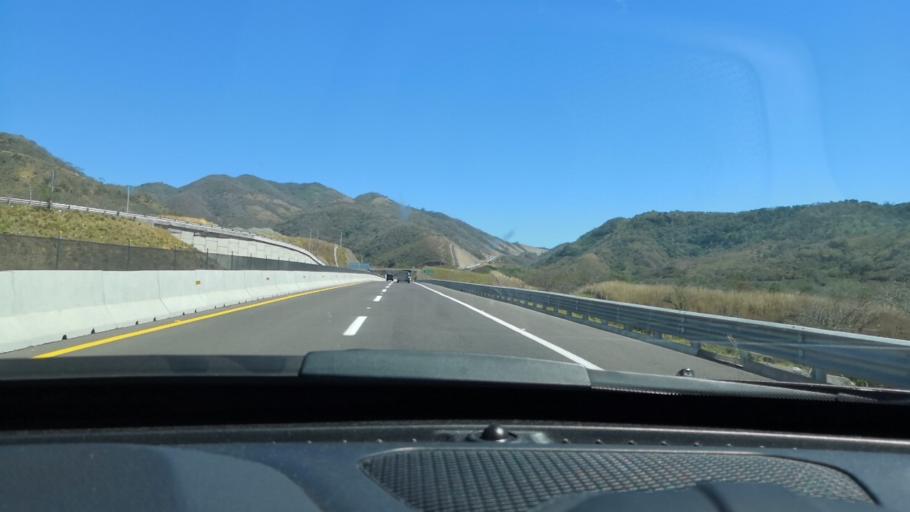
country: MX
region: Nayarit
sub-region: Compostela
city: Juan Escutia (Borbollon)
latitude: 21.1369
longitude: -104.9173
